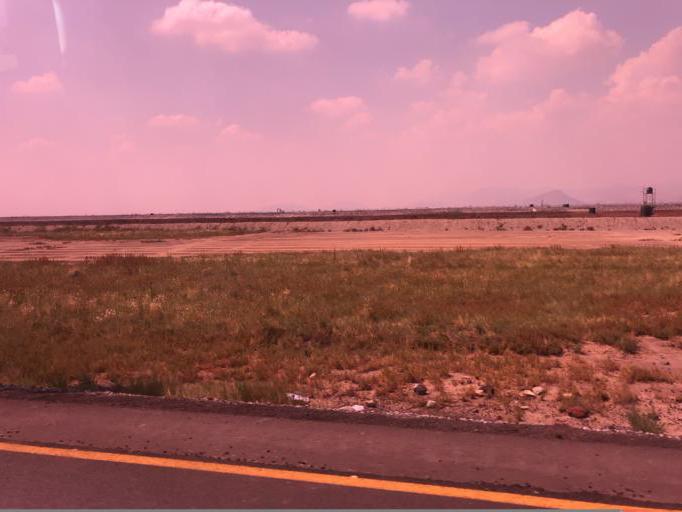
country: MX
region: Mexico
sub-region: Atenco
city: Colonia el Salado
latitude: 19.5377
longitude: -98.9852
